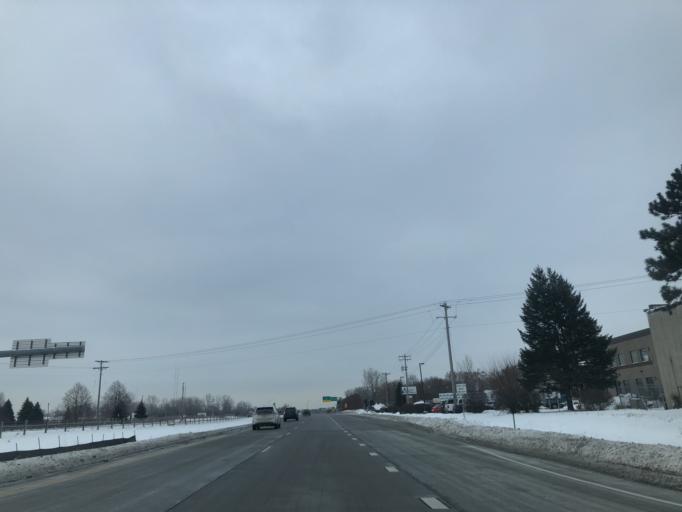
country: US
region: Minnesota
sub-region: Ramsey County
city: New Brighton
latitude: 45.0869
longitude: -93.1855
